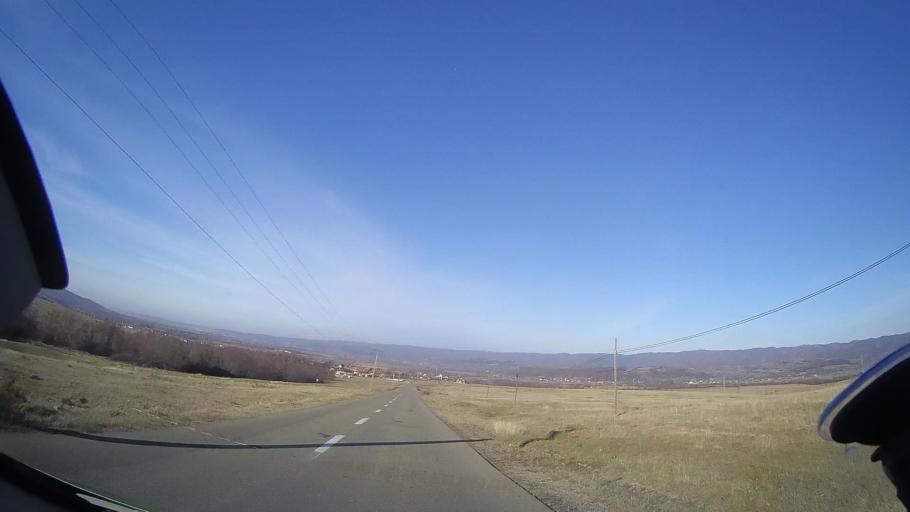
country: RO
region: Bihor
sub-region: Comuna Vadu Crisului
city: Vadu Crisului
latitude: 46.9791
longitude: 22.5329
